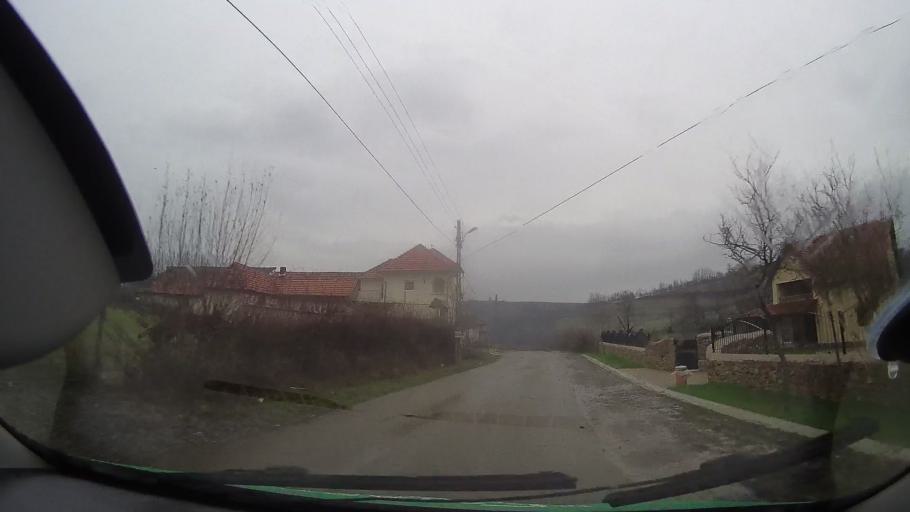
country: RO
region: Bihor
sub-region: Comuna Uileacu de Beius
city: Uileacu de Beius
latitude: 46.7071
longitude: 22.2237
